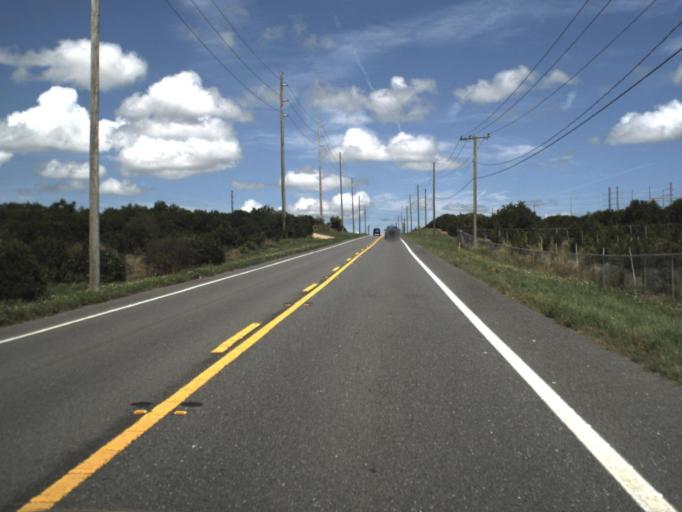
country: US
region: Florida
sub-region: Polk County
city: Dundee
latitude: 28.0015
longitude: -81.5949
